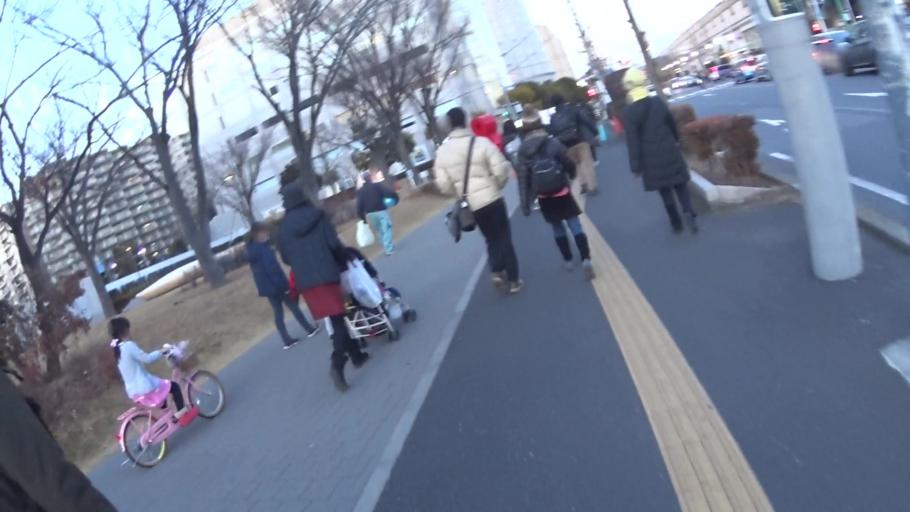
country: JP
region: Tokyo
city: Urayasu
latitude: 35.6472
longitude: 139.9098
